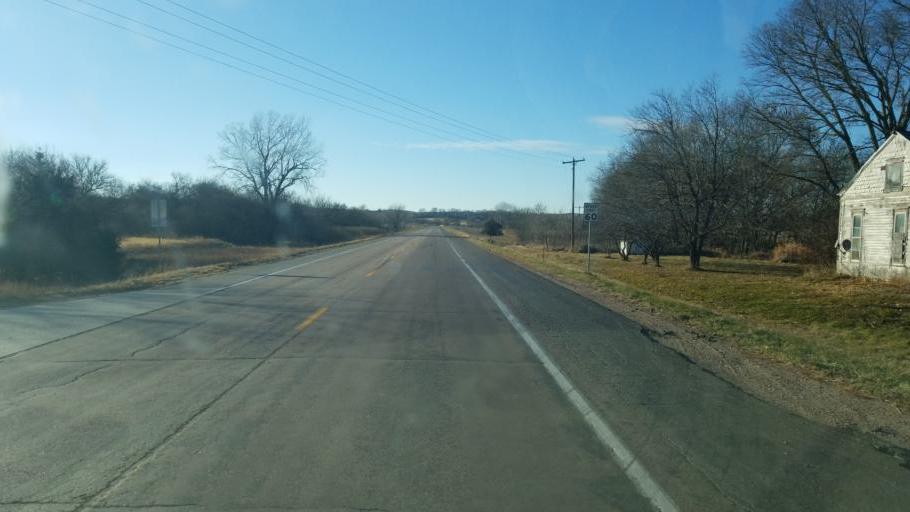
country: US
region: South Dakota
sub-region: Union County
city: Dakota Dunes
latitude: 42.4482
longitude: -96.5752
